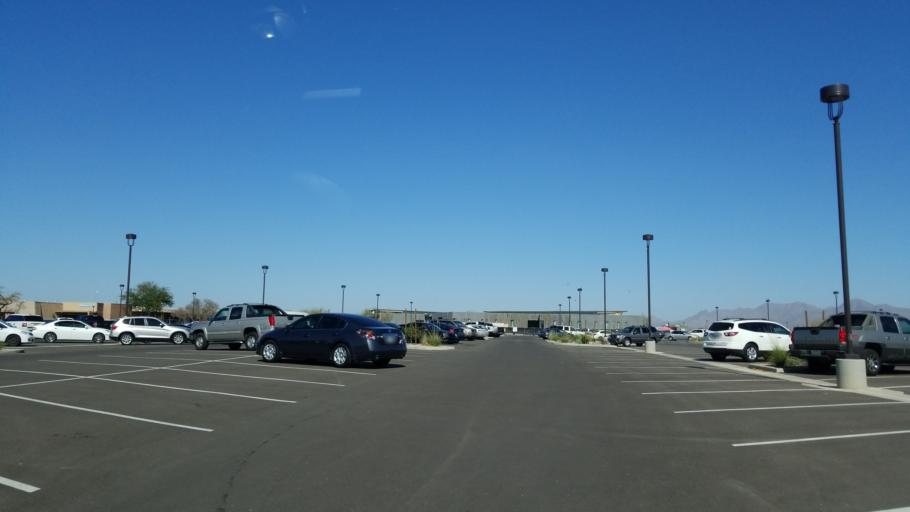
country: US
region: Arizona
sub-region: Maricopa County
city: Scottsdale
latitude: 33.5098
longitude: -111.8801
